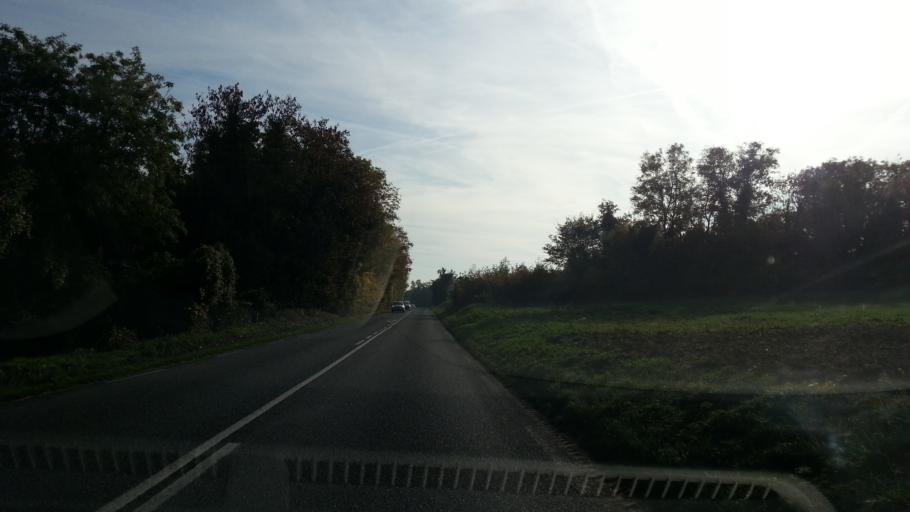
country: FR
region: Picardie
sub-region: Departement de l'Oise
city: Boran-sur-Oise
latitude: 49.1844
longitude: 2.3629
